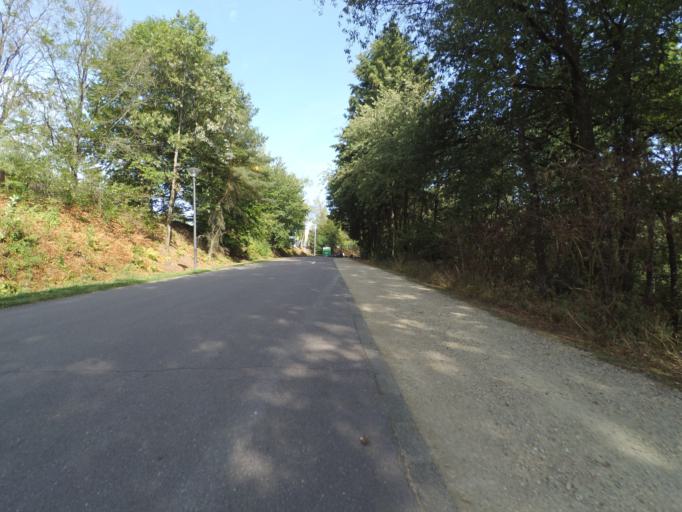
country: DE
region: Rheinland-Pfalz
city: Saarburg
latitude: 49.6192
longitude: 6.5438
